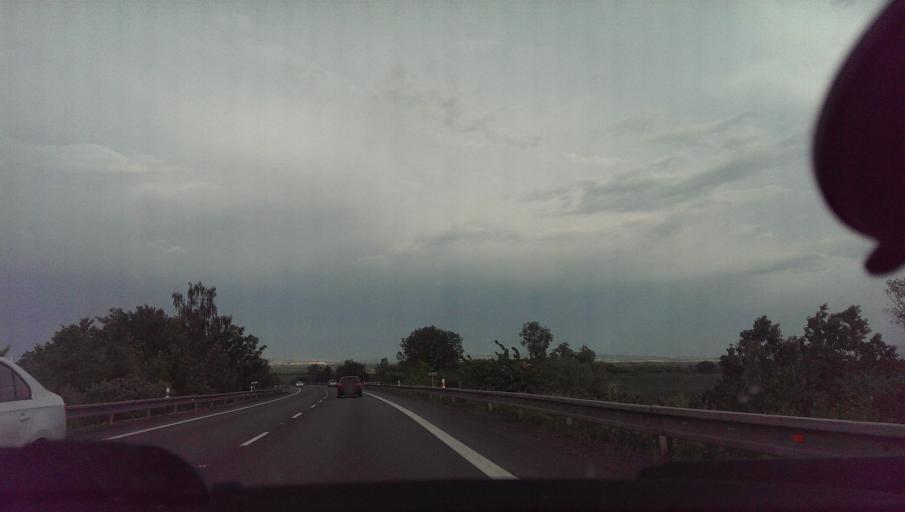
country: CZ
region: Zlin
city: Zlechov
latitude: 49.0670
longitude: 17.3777
